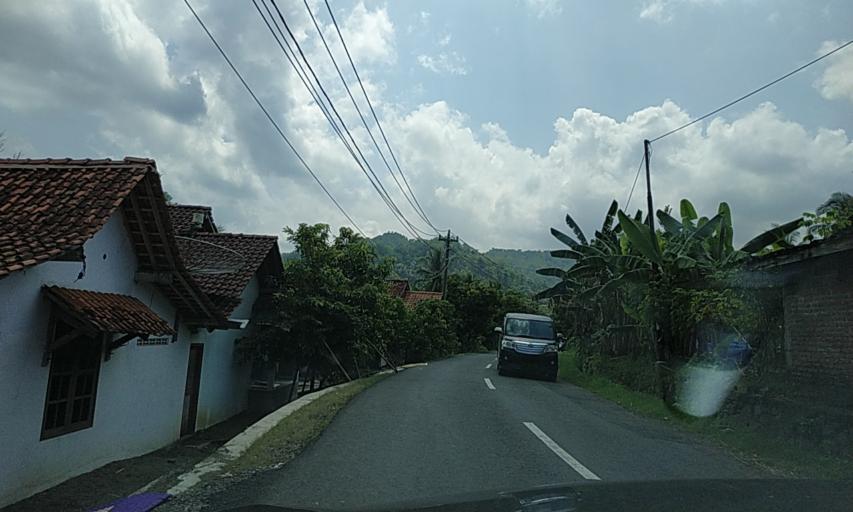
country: ID
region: Central Java
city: Kutoarjo
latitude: -7.6249
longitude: 109.7272
